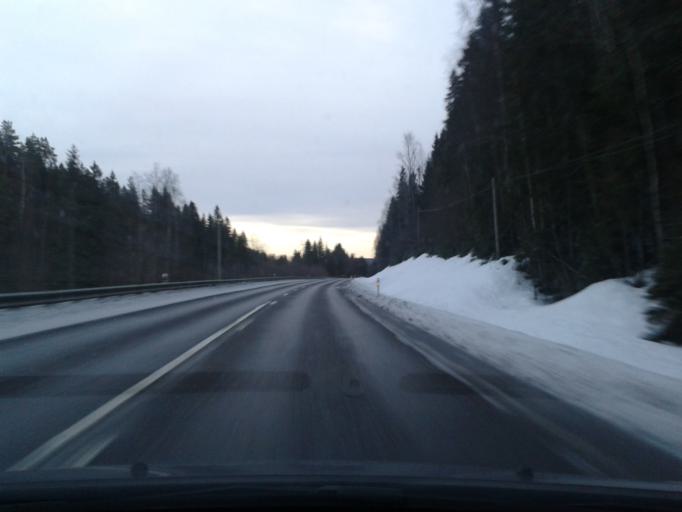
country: SE
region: Vaesternorrland
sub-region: Kramfors Kommun
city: Bollstabruk
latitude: 63.0966
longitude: 17.5234
